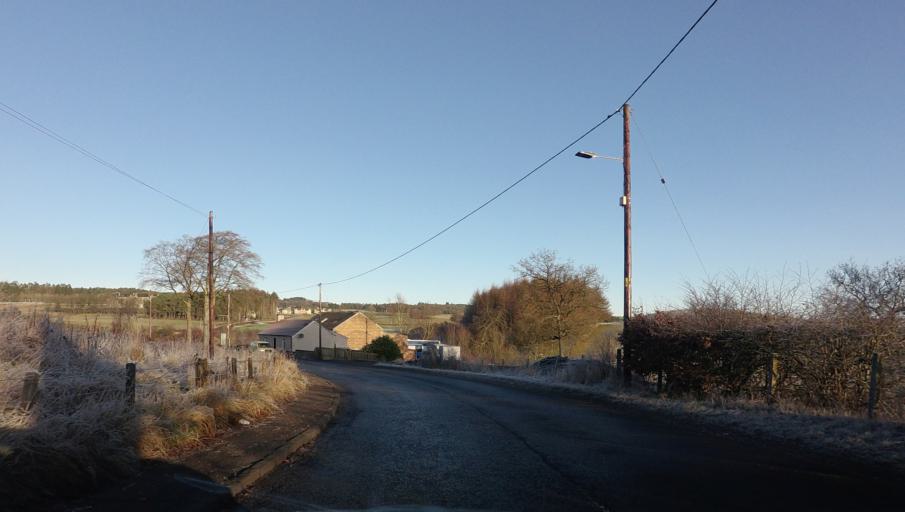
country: GB
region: Scotland
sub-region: North Lanarkshire
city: Shotts
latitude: 55.8023
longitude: -3.8396
